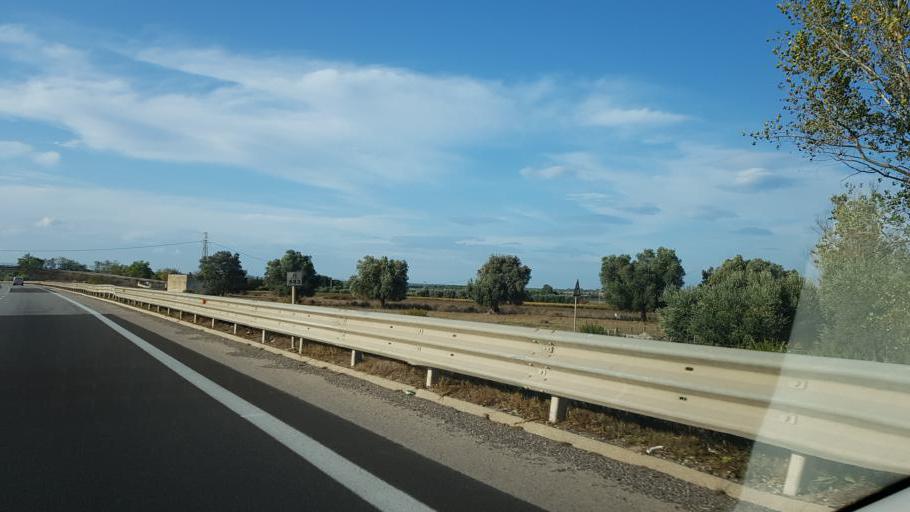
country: IT
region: Apulia
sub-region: Provincia di Brindisi
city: Francavilla Fontana
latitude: 40.5400
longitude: 17.6054
